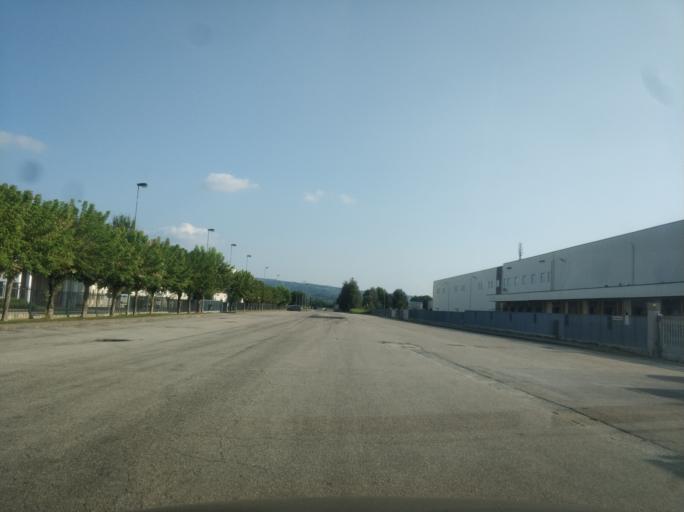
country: IT
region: Piedmont
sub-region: Provincia di Cuneo
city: Cinzano
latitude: 44.6937
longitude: 7.9002
